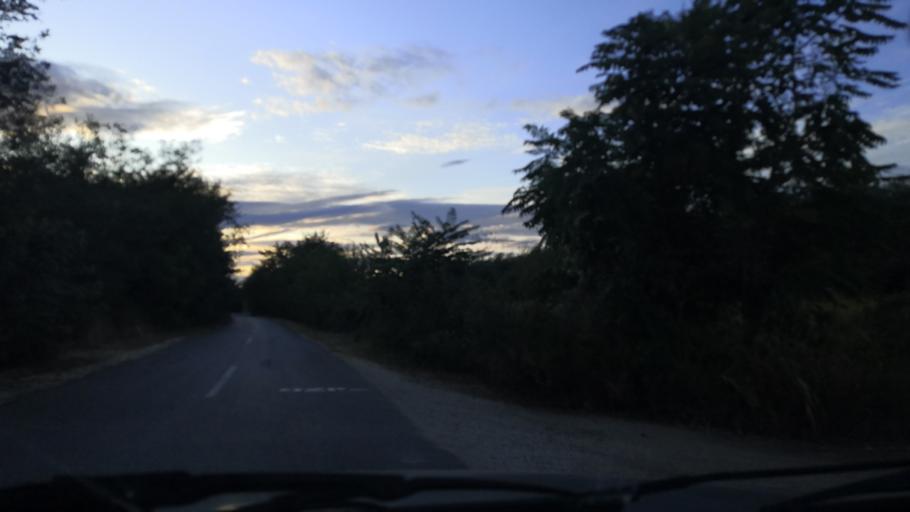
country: RO
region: Mehedinti
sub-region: Comuna Gruia
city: Izvoarele
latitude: 44.2811
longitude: 22.6451
